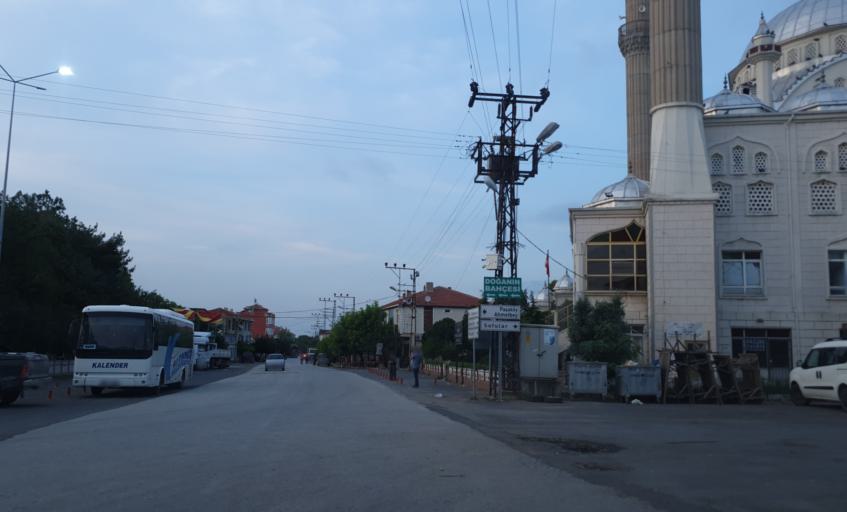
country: TR
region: Tekirdag
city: Beyazkoy
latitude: 41.3841
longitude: 27.6194
